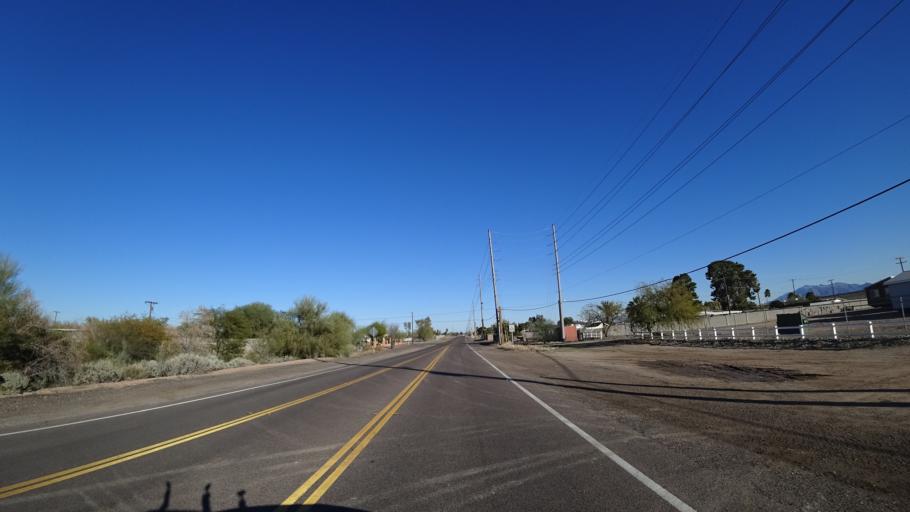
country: US
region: Arizona
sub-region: Maricopa County
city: Citrus Park
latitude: 33.4647
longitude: -112.4778
